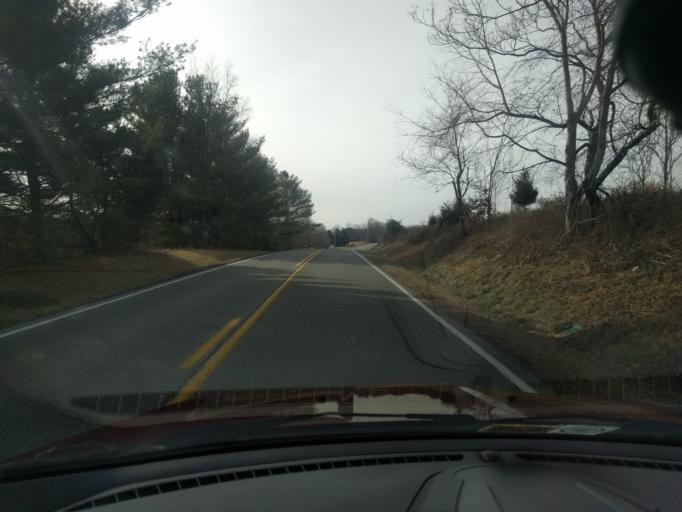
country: US
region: Virginia
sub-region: Augusta County
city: Stuarts Draft
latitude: 38.0340
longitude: -79.1169
